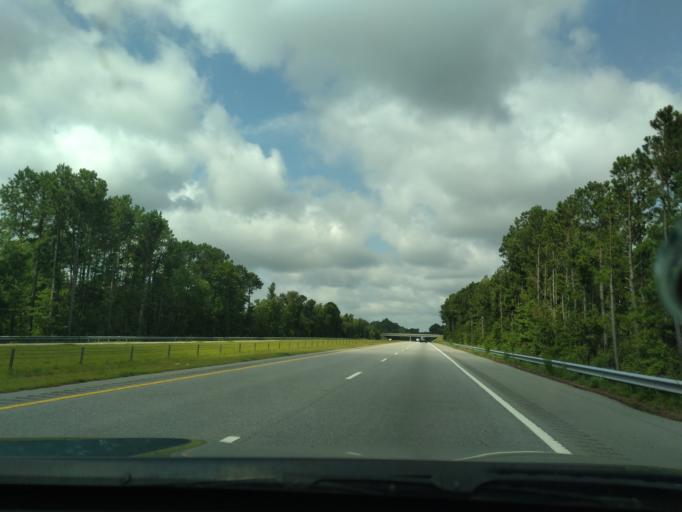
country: US
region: North Carolina
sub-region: Martin County
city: Williamston
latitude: 35.8268
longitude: -77.1477
